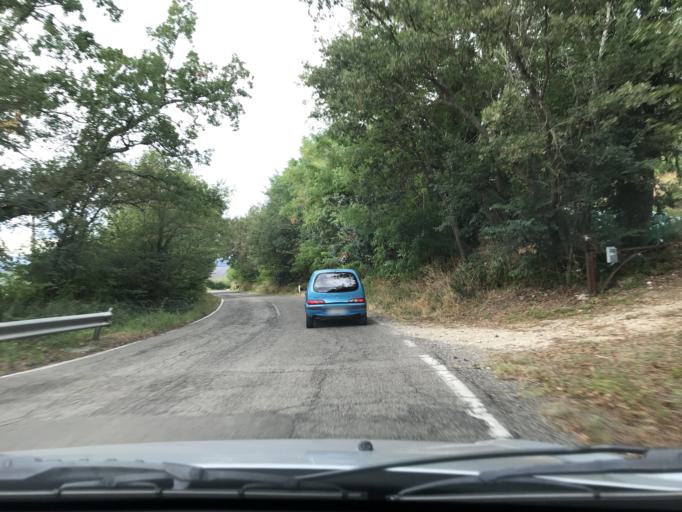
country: IT
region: Umbria
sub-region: Provincia di Terni
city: Montecchio
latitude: 42.6443
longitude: 12.2821
